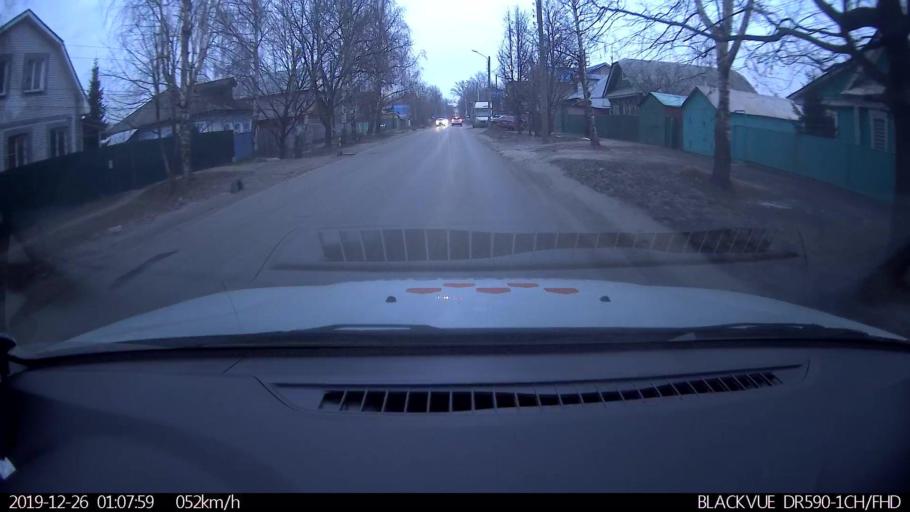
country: RU
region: Nizjnij Novgorod
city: Nizhniy Novgorod
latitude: 56.2857
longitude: 43.9123
